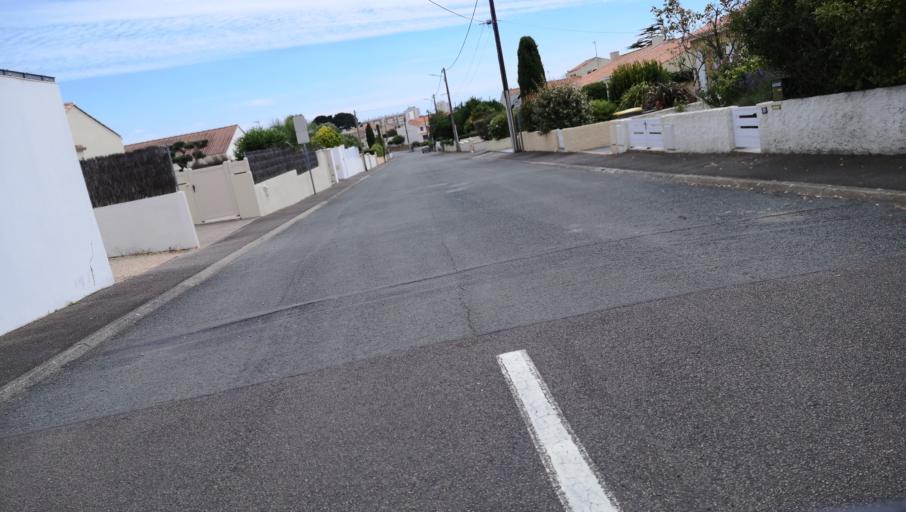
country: FR
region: Pays de la Loire
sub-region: Departement de la Vendee
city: Les Sables-d'Olonne
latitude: 46.5057
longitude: -1.7687
